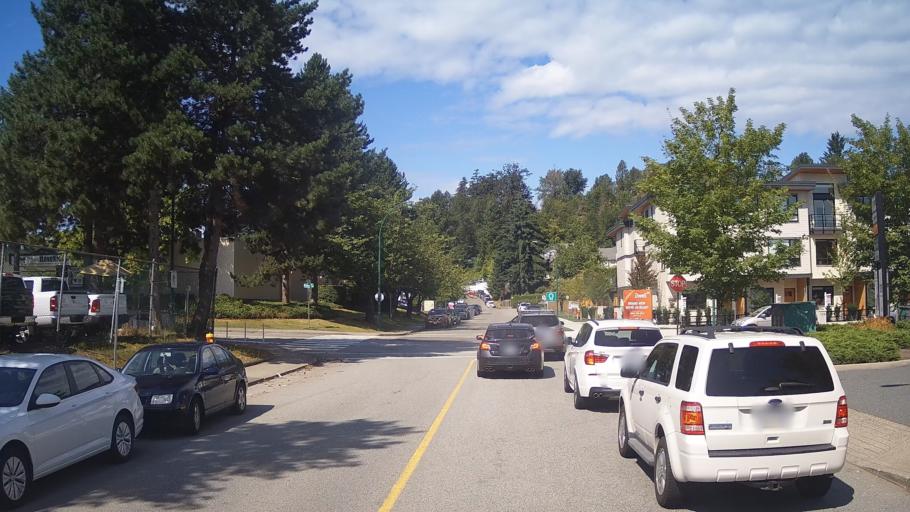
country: CA
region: British Columbia
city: Port Moody
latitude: 49.2789
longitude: -122.8178
